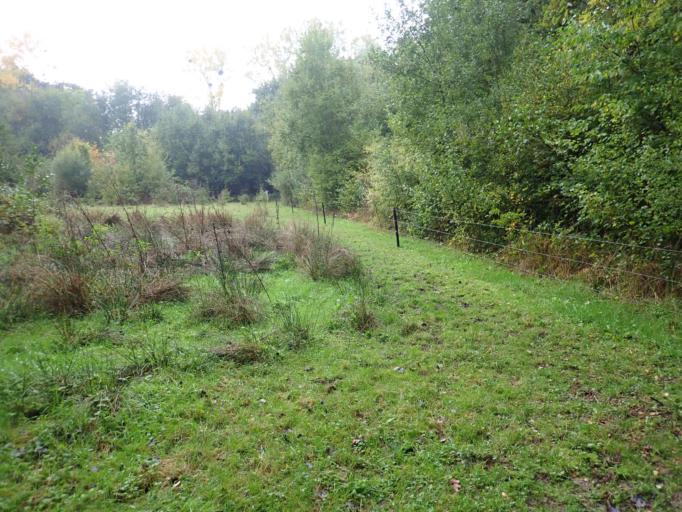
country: BE
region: Flanders
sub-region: Provincie Vlaams-Brabant
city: Aarschot
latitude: 50.9427
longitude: 4.8886
